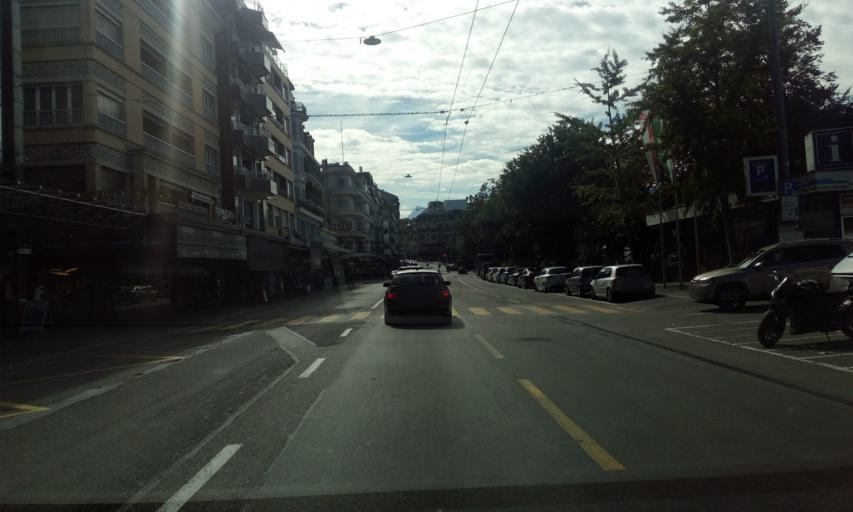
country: CH
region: Vaud
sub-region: Riviera-Pays-d'Enhaut District
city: Montreux
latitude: 46.4346
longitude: 6.9100
